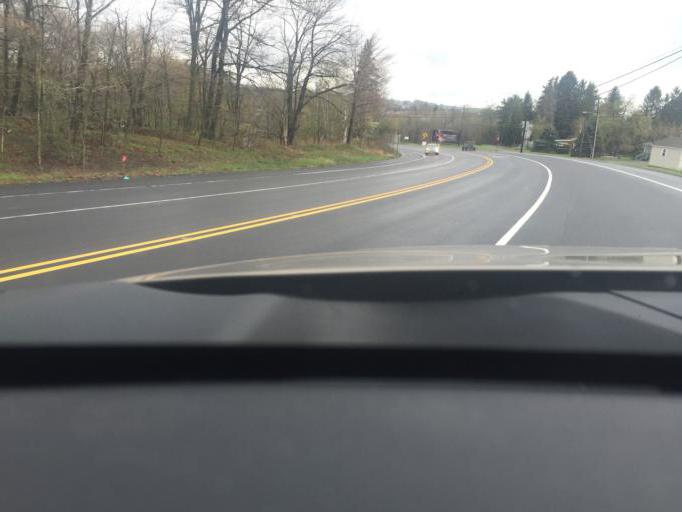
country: US
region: Pennsylvania
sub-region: Luzerne County
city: Harleigh
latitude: 40.9979
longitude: -75.9864
